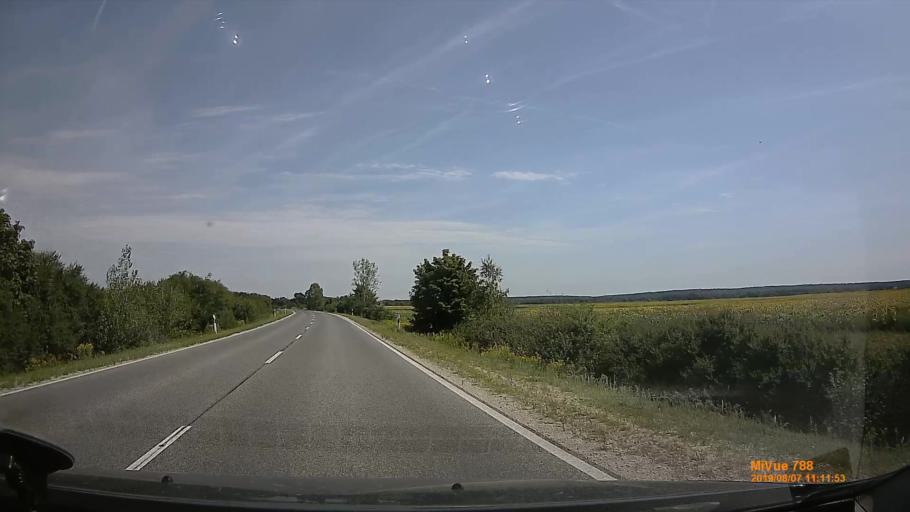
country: HU
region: Zala
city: Lenti
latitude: 46.6835
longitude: 16.5321
